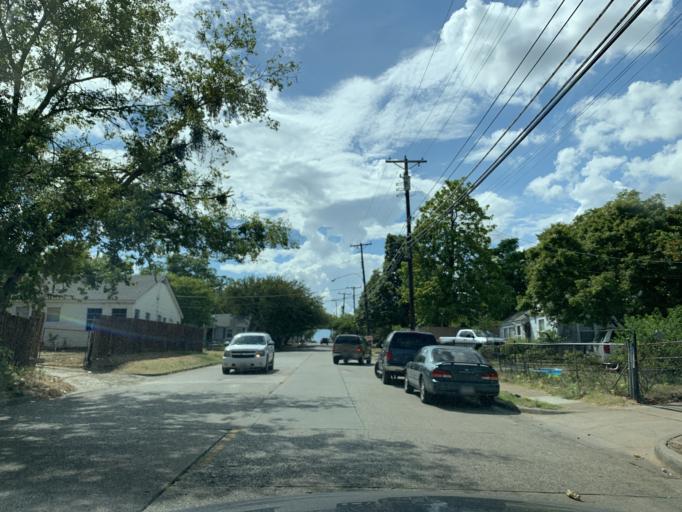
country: US
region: Texas
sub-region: Dallas County
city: Cockrell Hill
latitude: 32.7350
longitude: -96.8786
